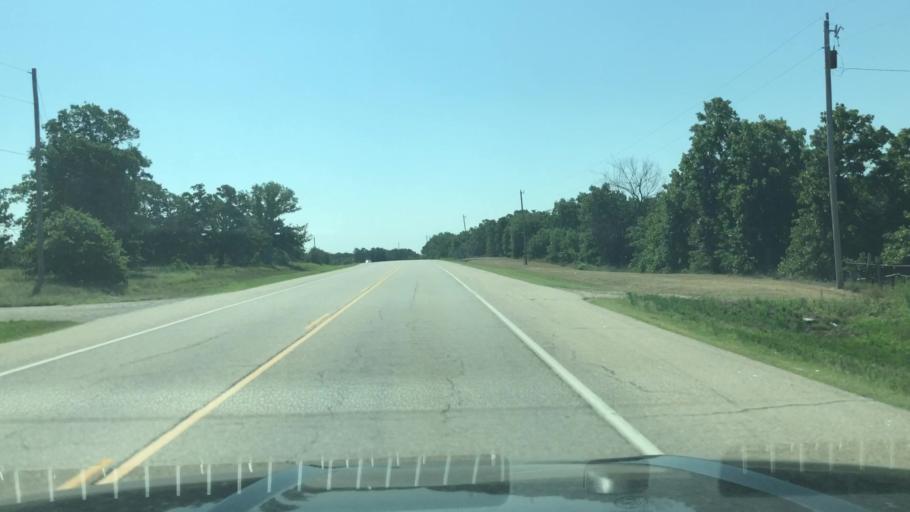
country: US
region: Oklahoma
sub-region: Creek County
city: Mannford
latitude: 35.9921
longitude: -96.3535
